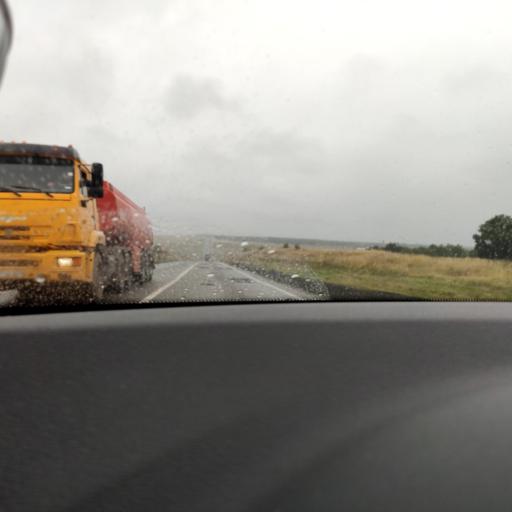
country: RU
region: Samara
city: Yelkhovka
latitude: 53.7302
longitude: 50.2317
